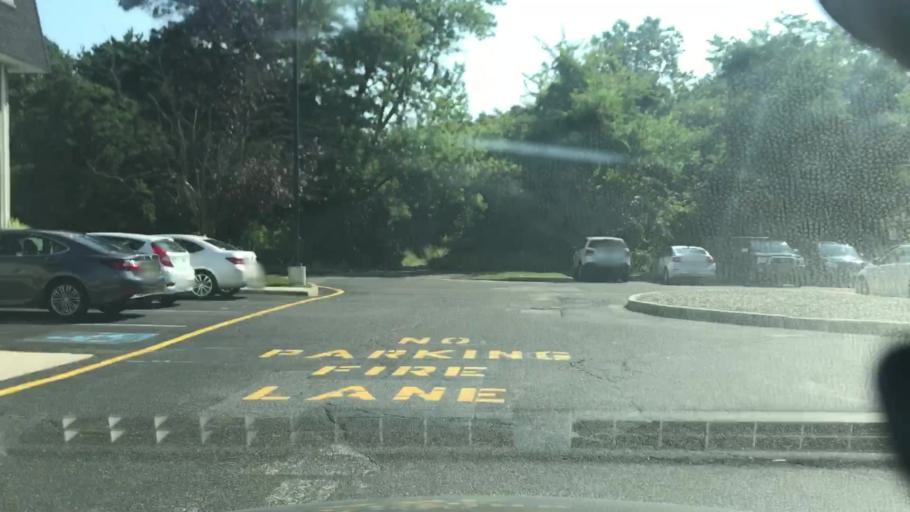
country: US
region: New Jersey
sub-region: Ocean County
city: Leisure Village East
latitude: 40.0562
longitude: -74.1522
